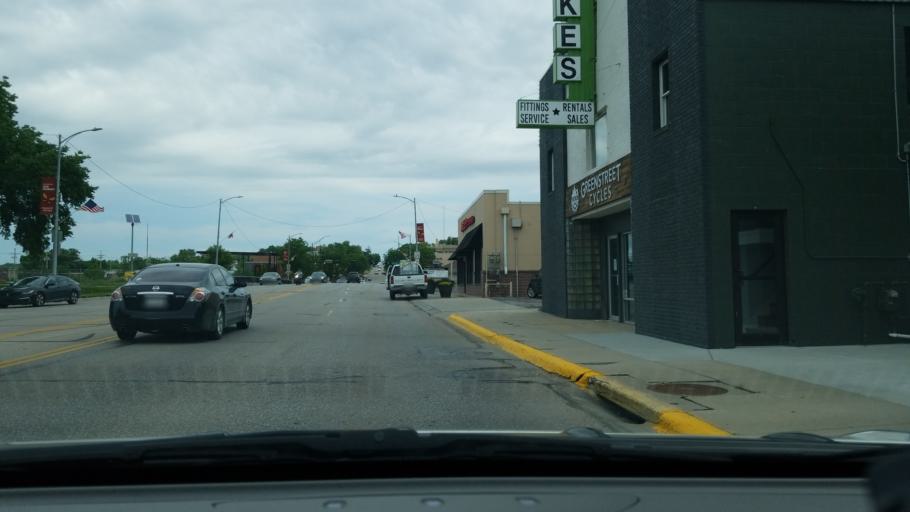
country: US
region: Nebraska
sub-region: Sarpy County
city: Papillion
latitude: 41.1549
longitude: -96.0429
